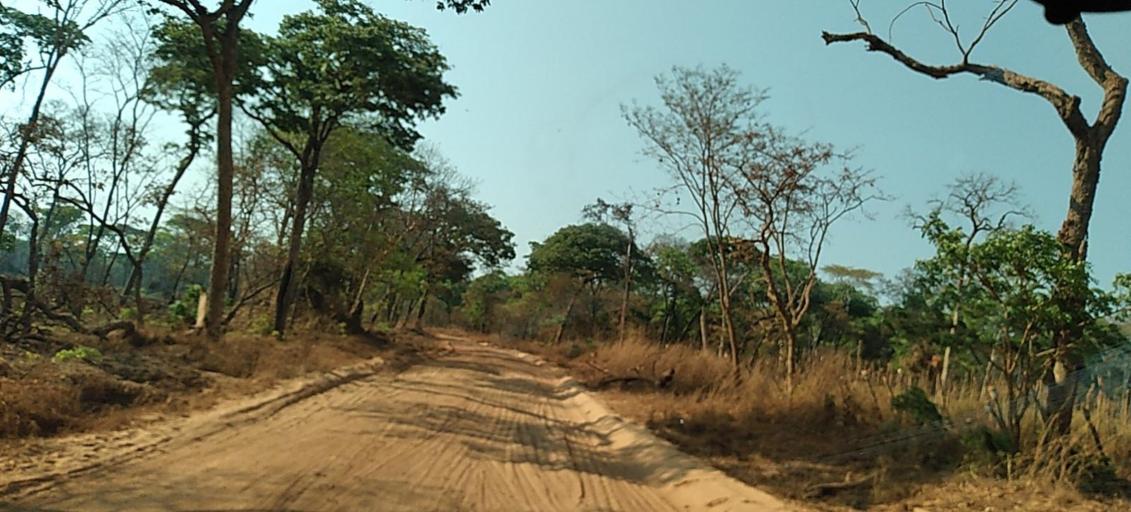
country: ZM
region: North-Western
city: Kasempa
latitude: -13.6727
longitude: 26.0177
